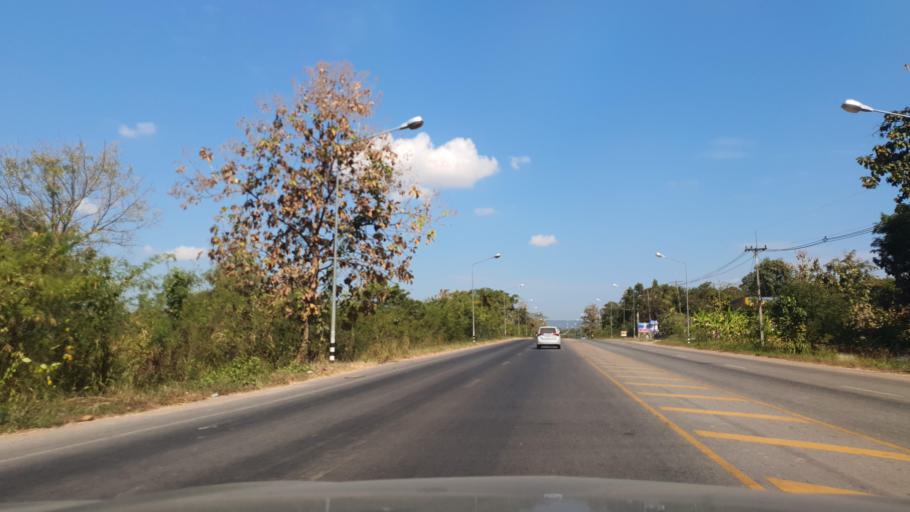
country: TH
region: Kalasin
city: Somdet
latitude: 16.7341
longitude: 103.7659
